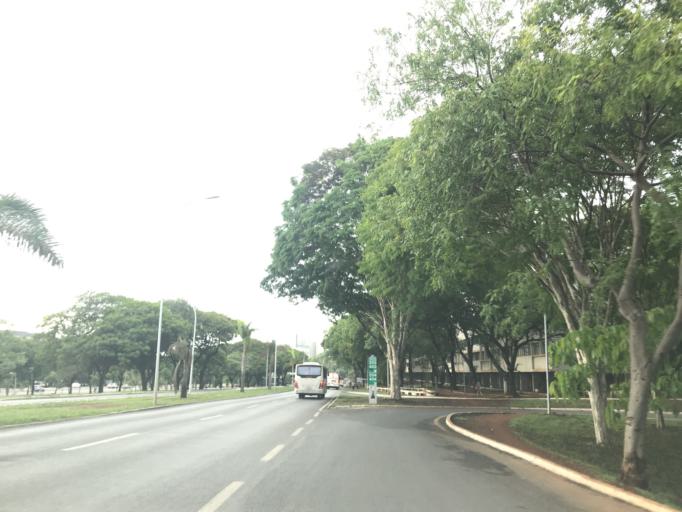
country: BR
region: Federal District
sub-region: Brasilia
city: Brasilia
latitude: -15.7771
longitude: -47.8817
